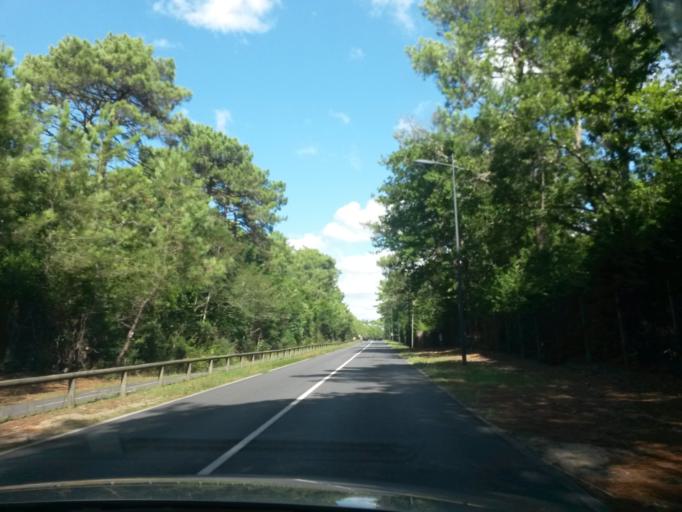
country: FR
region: Aquitaine
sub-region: Departement de la Gironde
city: Ares
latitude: 44.7380
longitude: -1.1933
